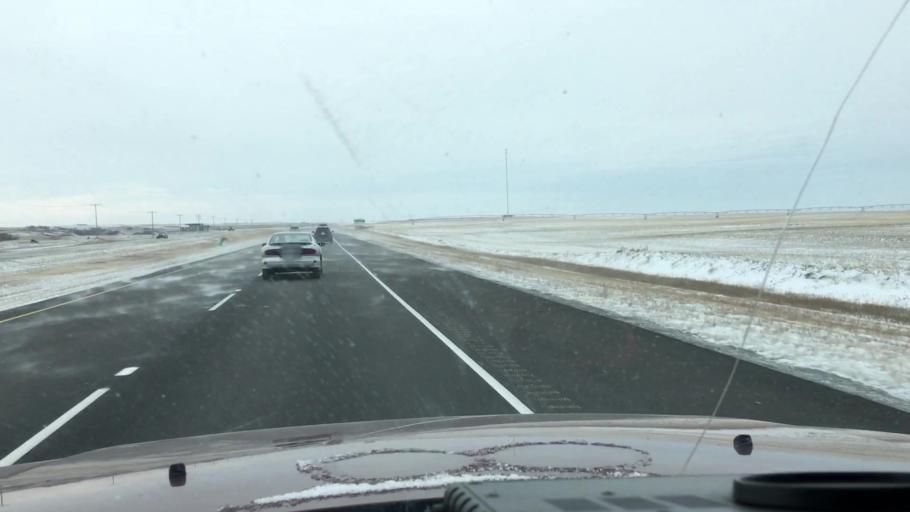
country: CA
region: Saskatchewan
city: Saskatoon
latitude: 51.7480
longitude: -106.4764
